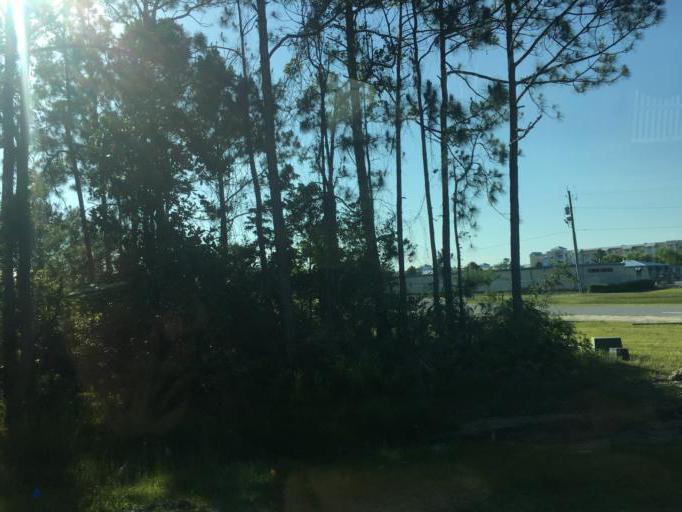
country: US
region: Florida
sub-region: Bay County
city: Panama City Beach
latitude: 30.1949
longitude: -85.8244
